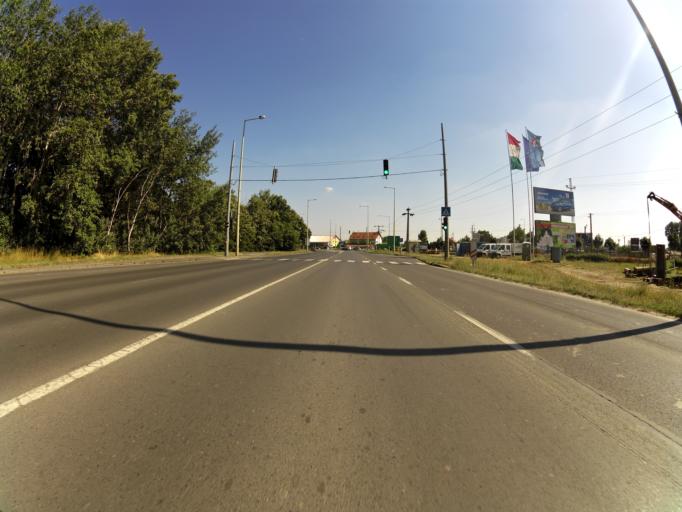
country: HU
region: Csongrad
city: Szeged
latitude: 46.2691
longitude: 20.1034
